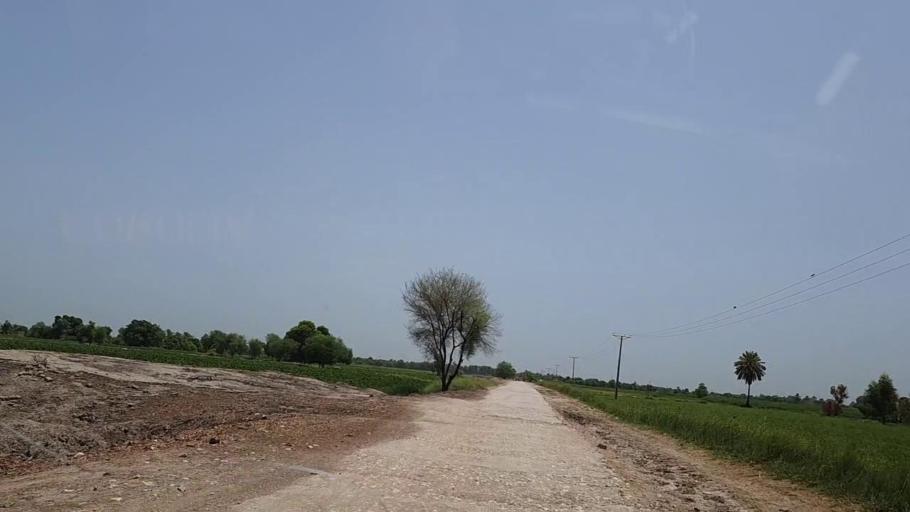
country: PK
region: Sindh
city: Tharu Shah
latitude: 26.9522
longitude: 68.0888
